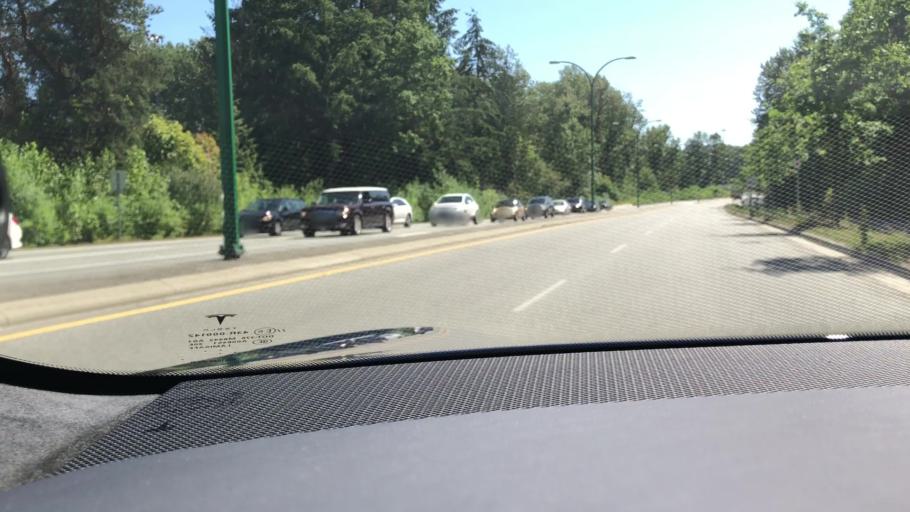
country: CA
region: British Columbia
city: Burnaby
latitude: 49.2496
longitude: -122.9666
